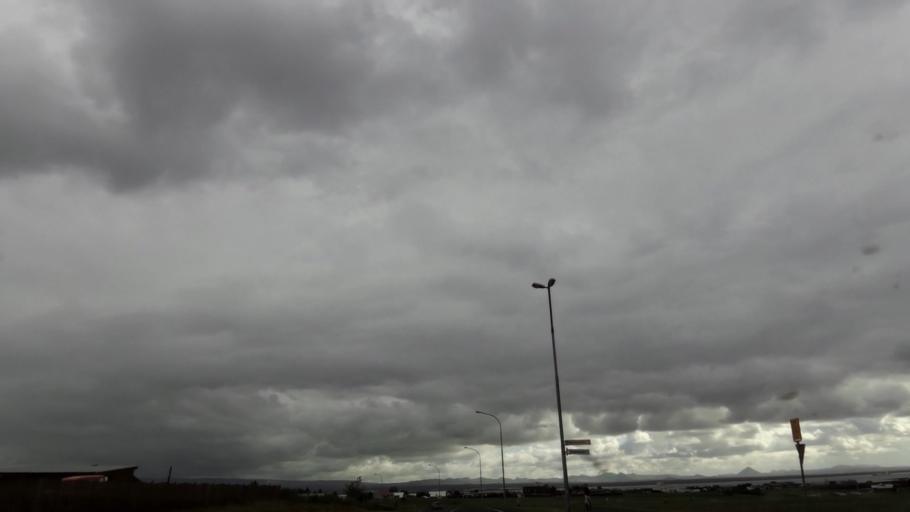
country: IS
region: Capital Region
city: Alftanes
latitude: 64.1018
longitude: -22.0268
